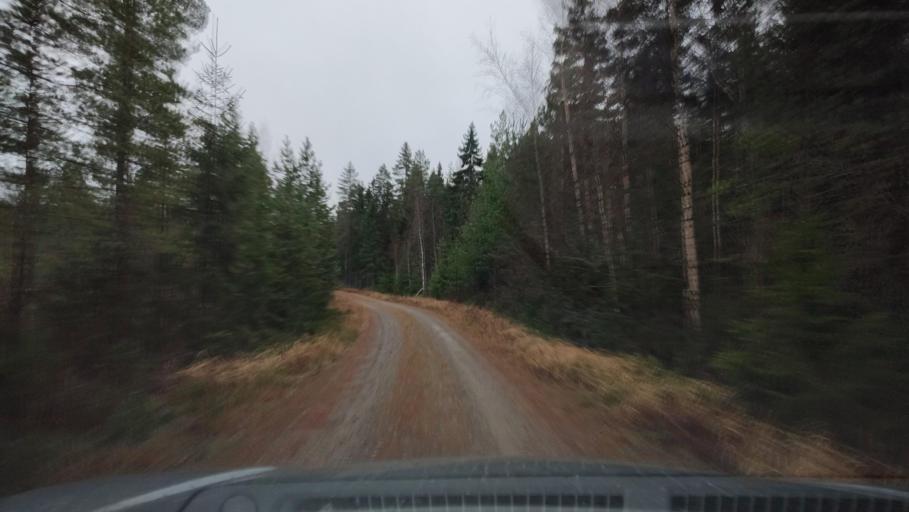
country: FI
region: Southern Ostrobothnia
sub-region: Suupohja
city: Karijoki
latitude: 62.1575
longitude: 21.5896
